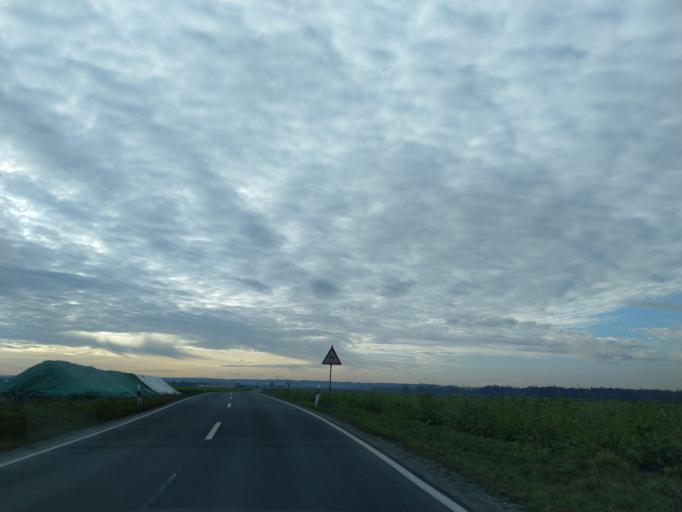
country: DE
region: Bavaria
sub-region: Lower Bavaria
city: Moos
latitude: 48.7331
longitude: 12.9410
